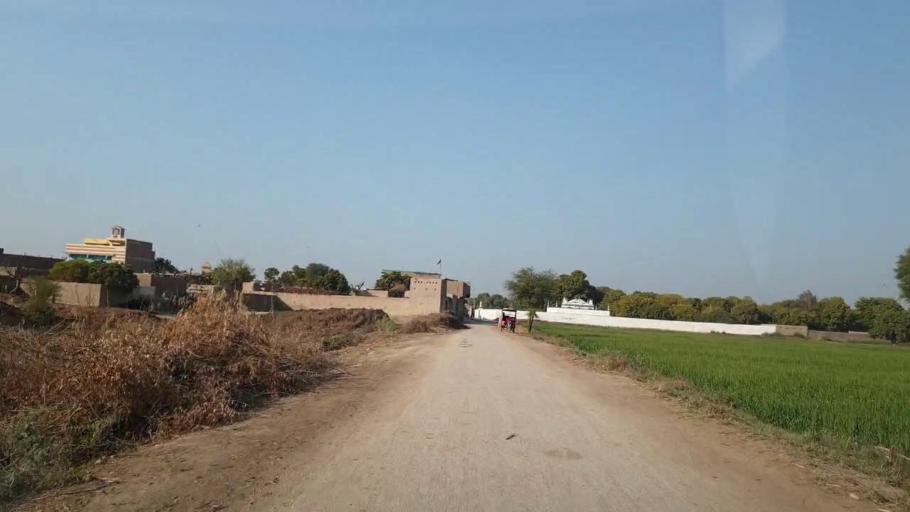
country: PK
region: Sindh
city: Tando Jam
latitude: 25.4714
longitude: 68.5407
